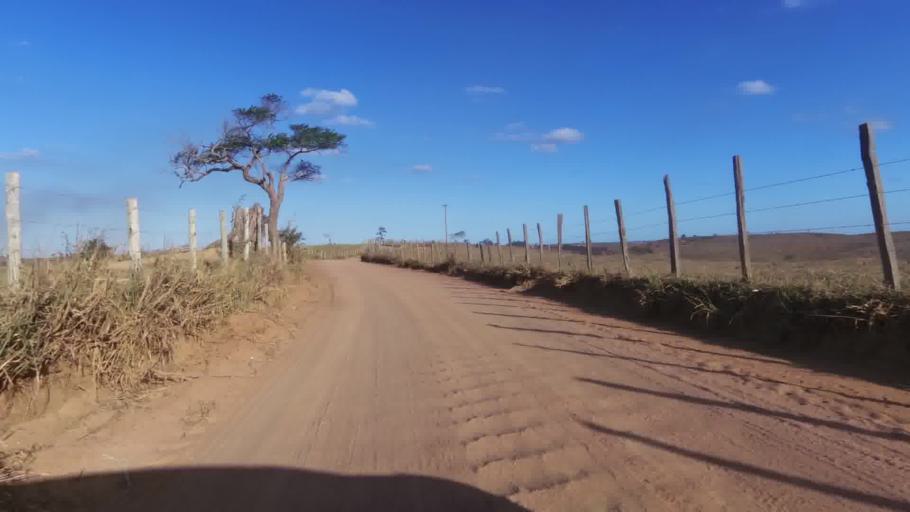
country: BR
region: Espirito Santo
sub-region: Marataizes
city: Marataizes
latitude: -21.1507
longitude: -41.0656
